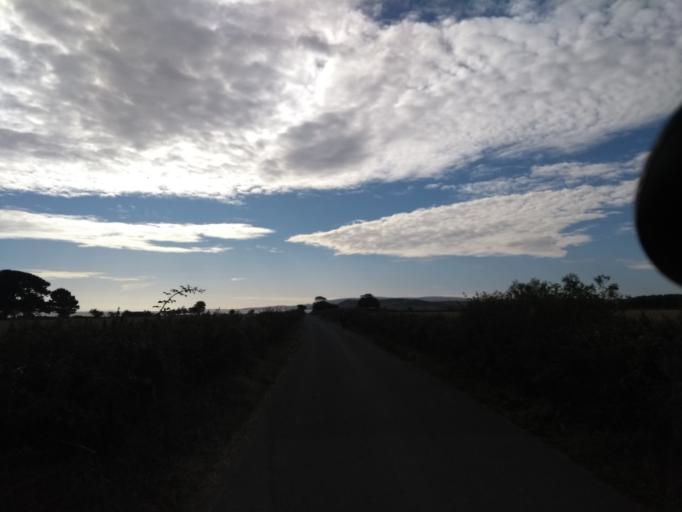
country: GB
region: England
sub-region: Somerset
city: Minehead
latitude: 51.1918
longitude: -3.4320
